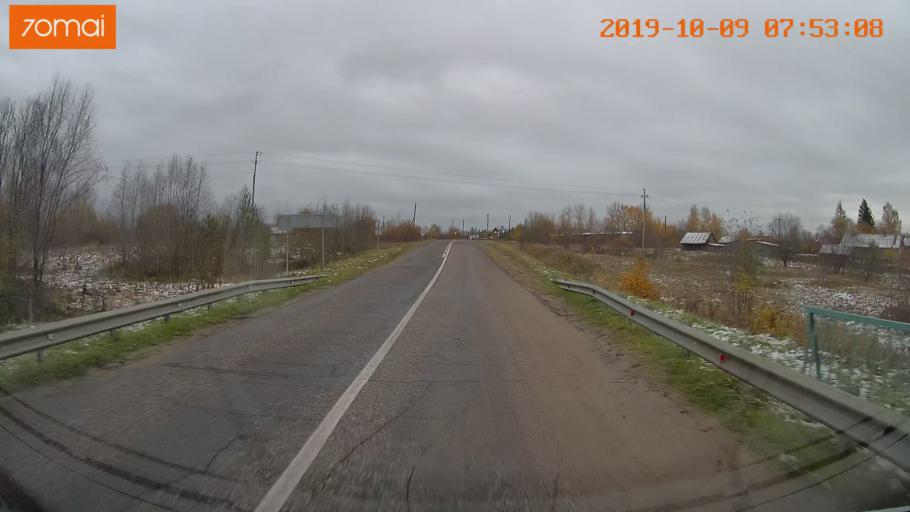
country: RU
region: Jaroslavl
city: Kukoboy
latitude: 58.6964
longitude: 39.8925
